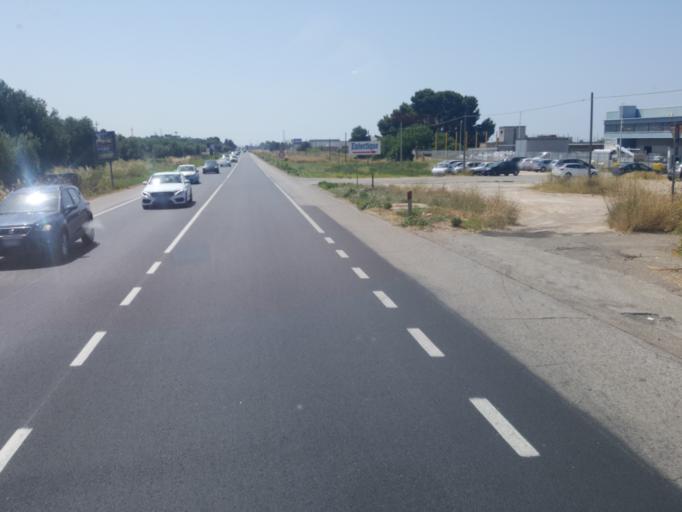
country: IT
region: Apulia
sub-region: Provincia di Taranto
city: Massafra
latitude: 40.5729
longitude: 17.1215
